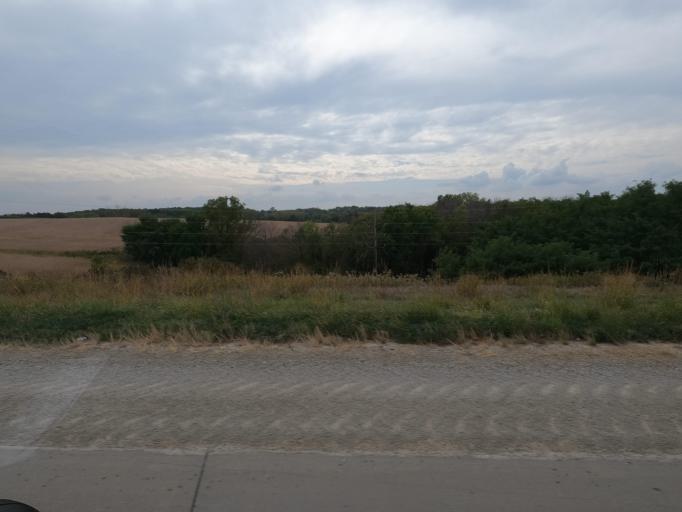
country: US
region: Iowa
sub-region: Marion County
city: Pella
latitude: 41.3910
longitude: -92.9258
